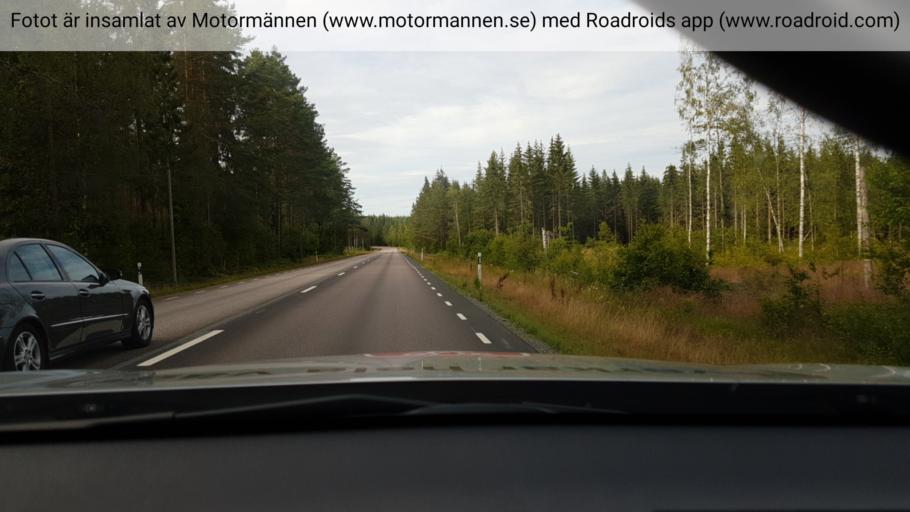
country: SE
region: Vaestra Goetaland
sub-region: Amals Kommun
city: Amal
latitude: 59.0647
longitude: 12.6535
